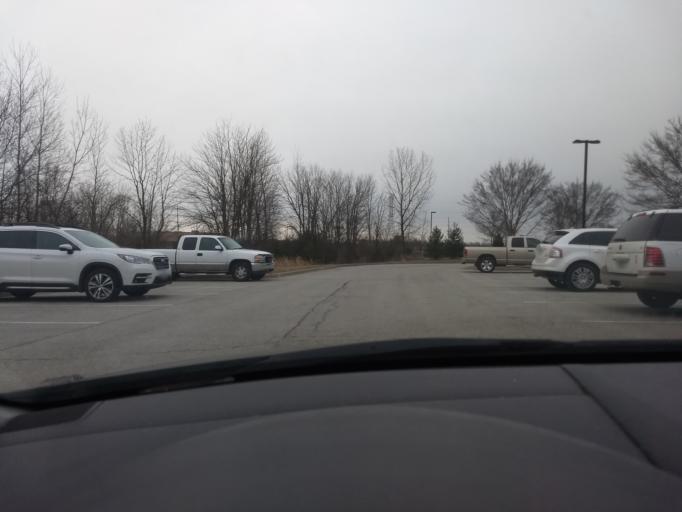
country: US
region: Indiana
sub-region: Clark County
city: Clarksville
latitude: 38.3339
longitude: -85.7520
